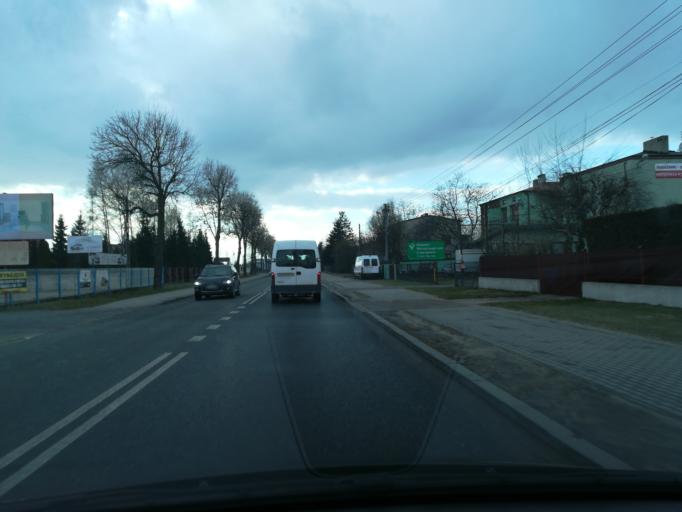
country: PL
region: Lodz Voivodeship
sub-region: Powiat radomszczanski
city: Radomsko
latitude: 51.0731
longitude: 19.4169
